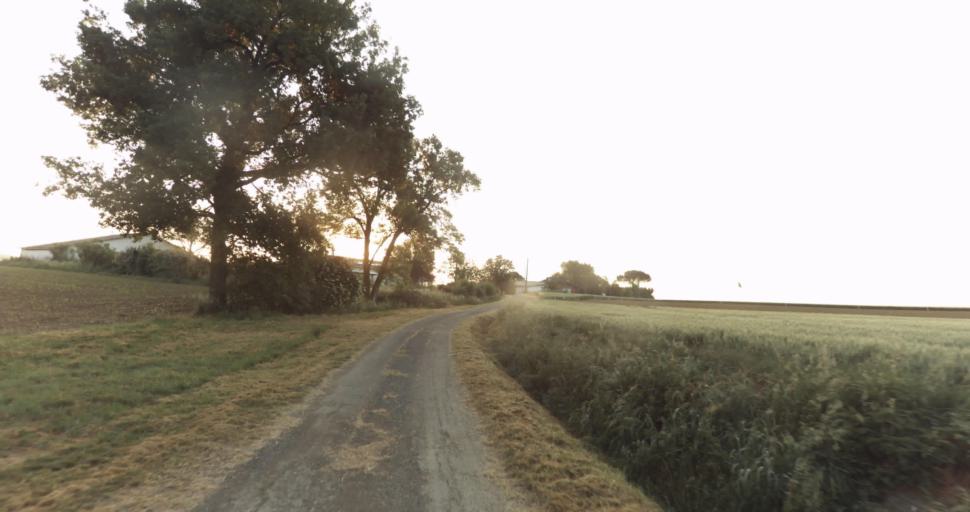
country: FR
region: Midi-Pyrenees
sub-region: Departement du Gers
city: Pujaudran
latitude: 43.6554
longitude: 1.0991
